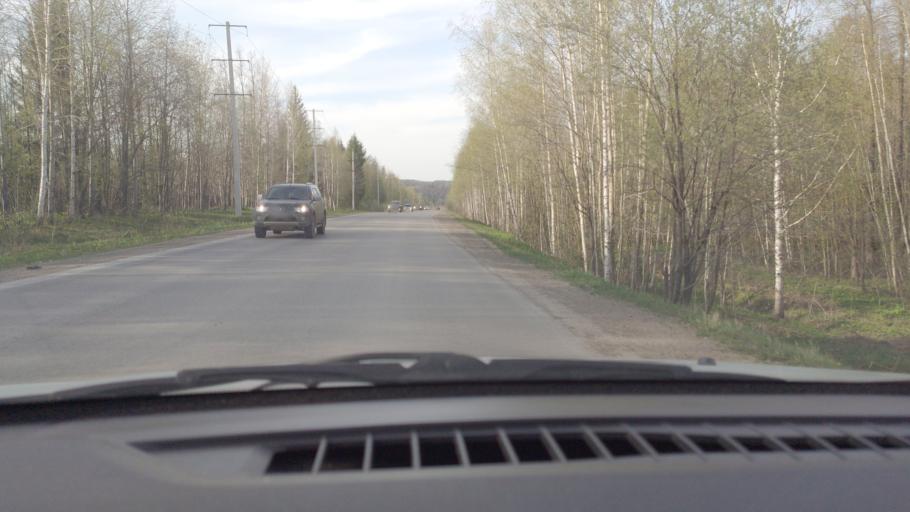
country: RU
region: Perm
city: Novyye Lyady
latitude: 57.9443
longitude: 56.5687
